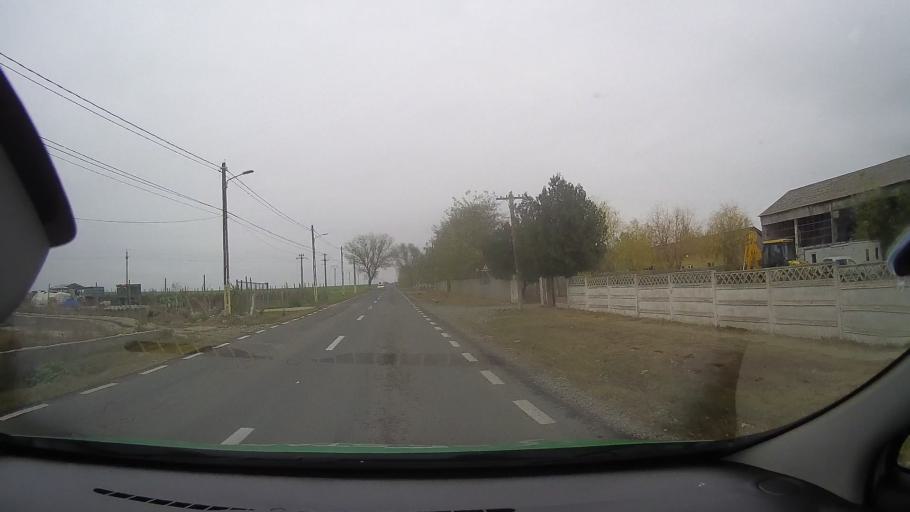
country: RO
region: Constanta
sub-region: Comuna Tortoman
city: Tortoman
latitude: 44.3492
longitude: 28.2181
